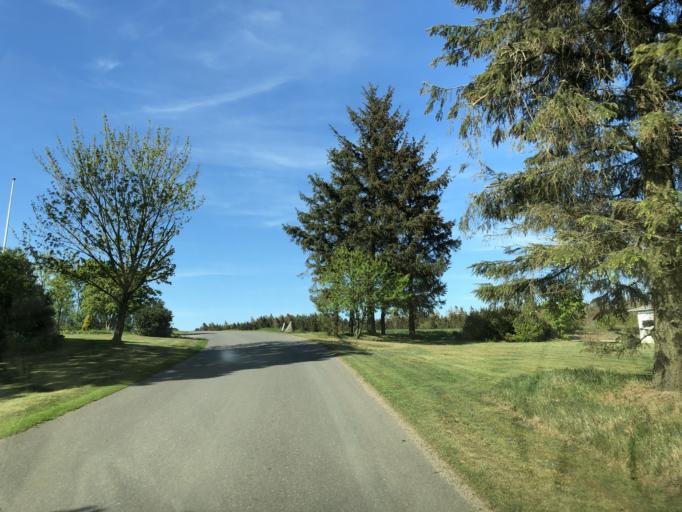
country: DK
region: Central Jutland
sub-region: Ringkobing-Skjern Kommune
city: Videbaek
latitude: 56.1952
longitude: 8.5117
